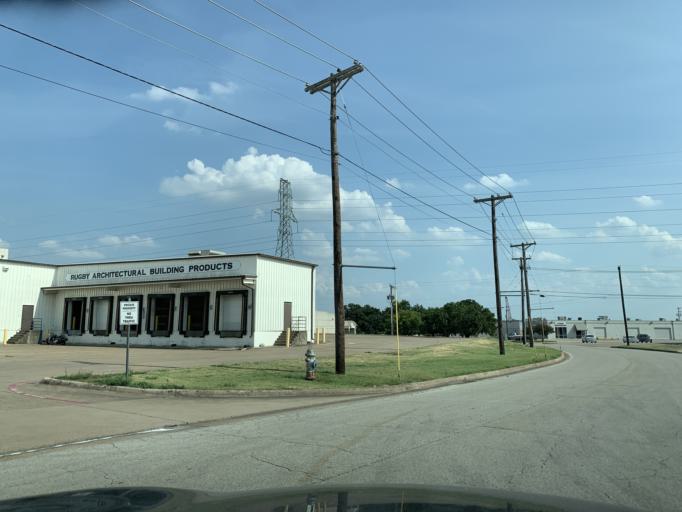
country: US
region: Texas
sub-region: Tarrant County
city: Richland Hills
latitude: 32.8071
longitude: -97.2170
